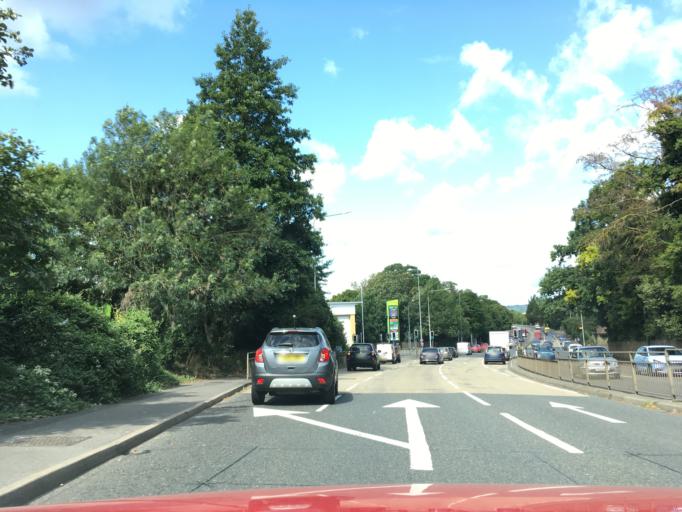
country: GB
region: England
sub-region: Kent
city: Aylesford
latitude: 51.2935
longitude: 0.4731
